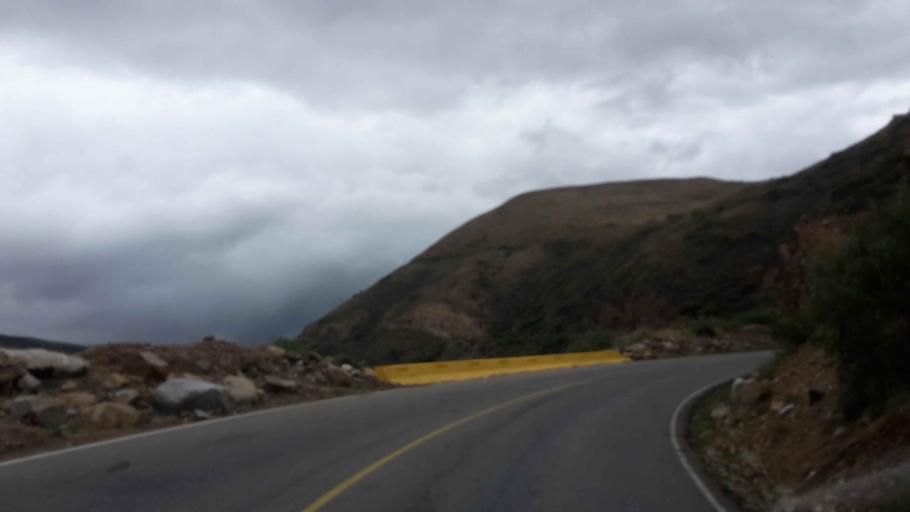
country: BO
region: Cochabamba
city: Punata
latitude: -17.5020
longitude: -65.7971
